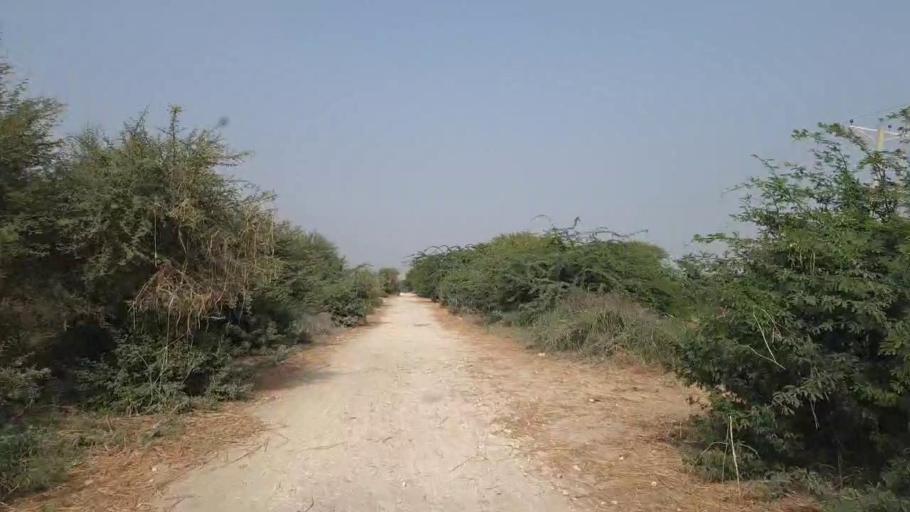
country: PK
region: Sindh
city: Kario
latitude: 24.9298
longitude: 68.6009
